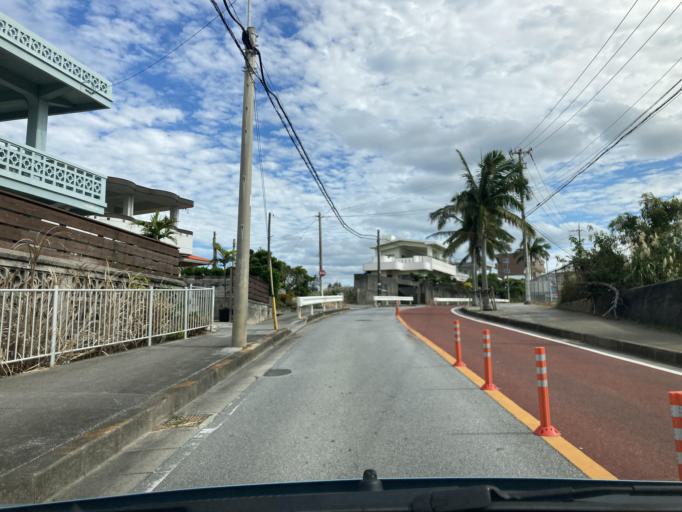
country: JP
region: Okinawa
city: Ishikawa
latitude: 26.4390
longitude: 127.7722
